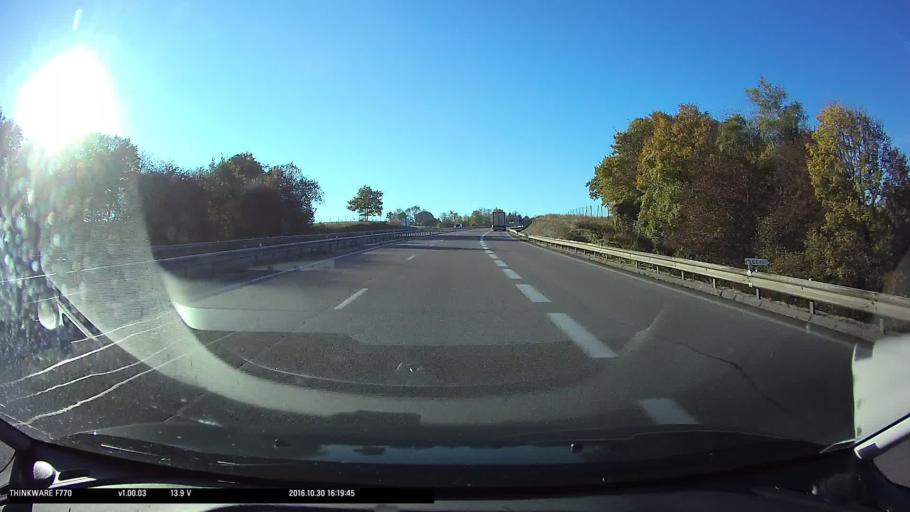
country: FR
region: Franche-Comte
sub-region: Departement du Doubs
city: Clerval
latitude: 47.4057
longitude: 6.4684
